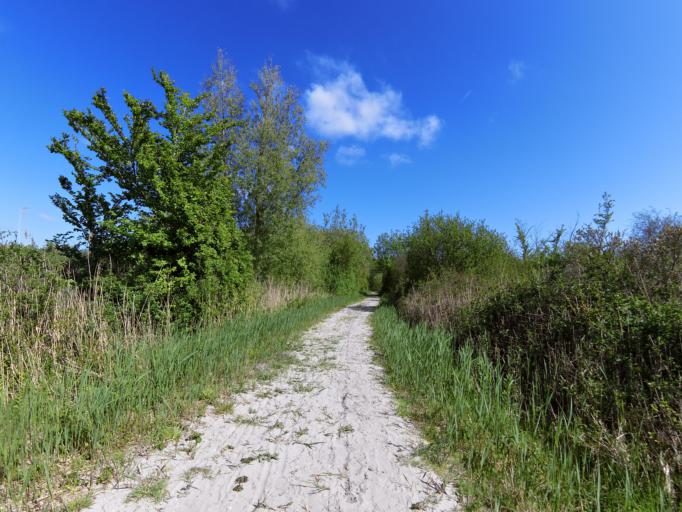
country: NL
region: South Holland
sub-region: Gemeente Goeree-Overflakkee
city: Ouddorp
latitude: 51.7856
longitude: 3.8932
